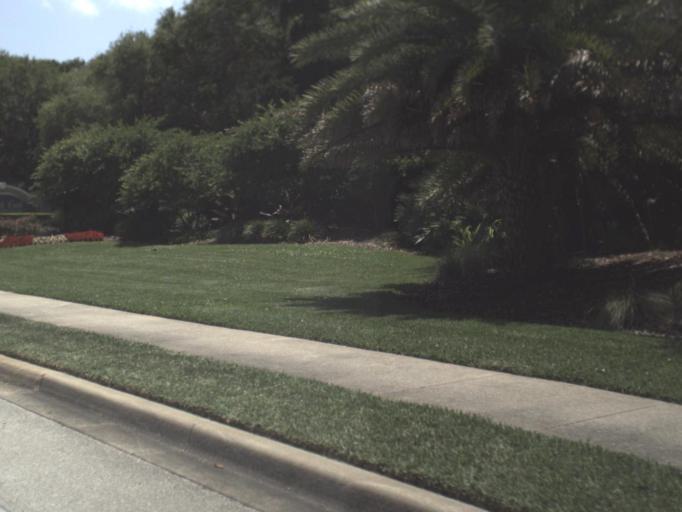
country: US
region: Florida
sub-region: Saint Johns County
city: Saint Augustine Beach
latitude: 29.8321
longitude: -81.2738
